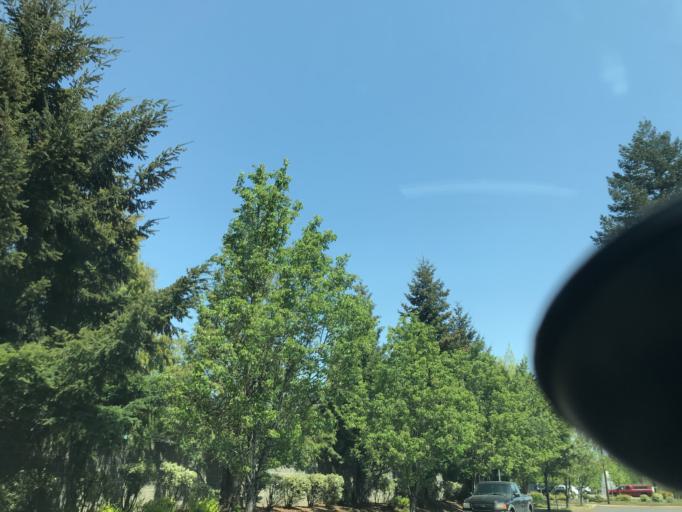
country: US
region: Oregon
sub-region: Multnomah County
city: Lents
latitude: 45.4944
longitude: -122.5627
